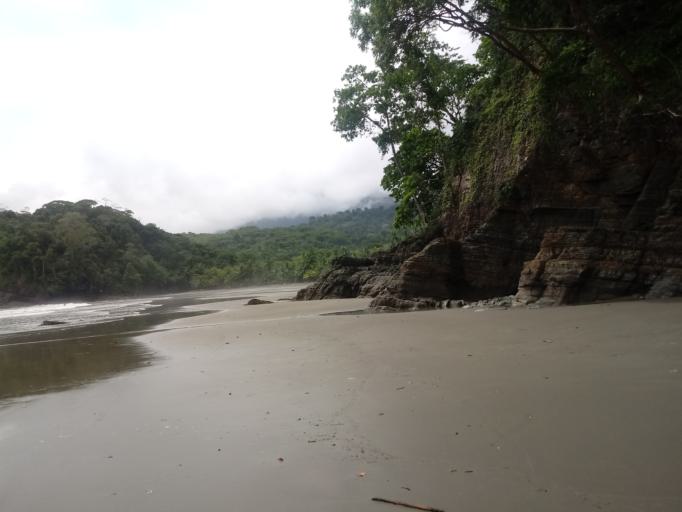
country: CR
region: San Jose
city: Mercedes
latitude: 9.0882
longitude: -83.6771
